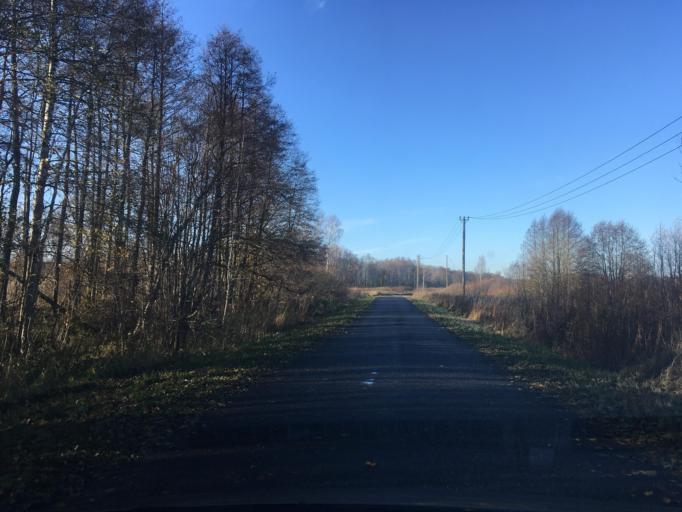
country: EE
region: Harju
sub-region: Maardu linn
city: Maardu
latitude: 59.4762
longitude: 25.1176
